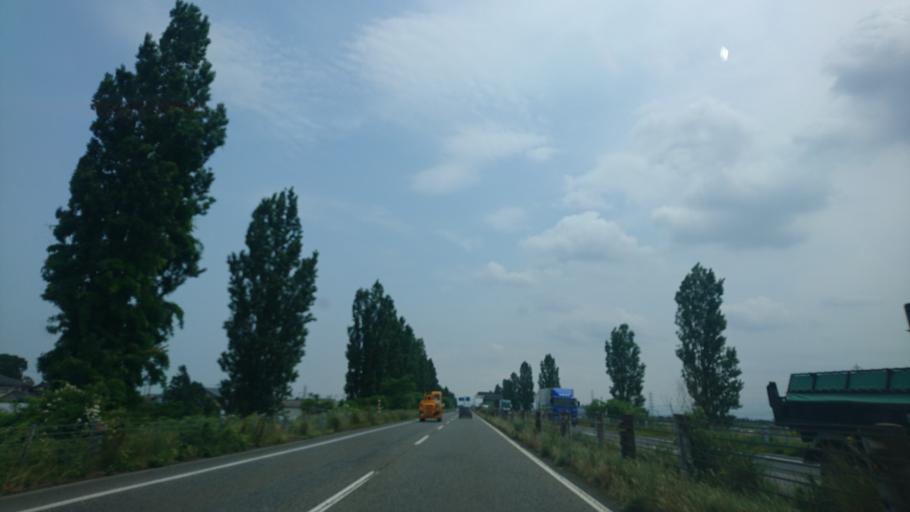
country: JP
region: Niigata
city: Kameda-honcho
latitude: 37.9377
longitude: 139.1727
